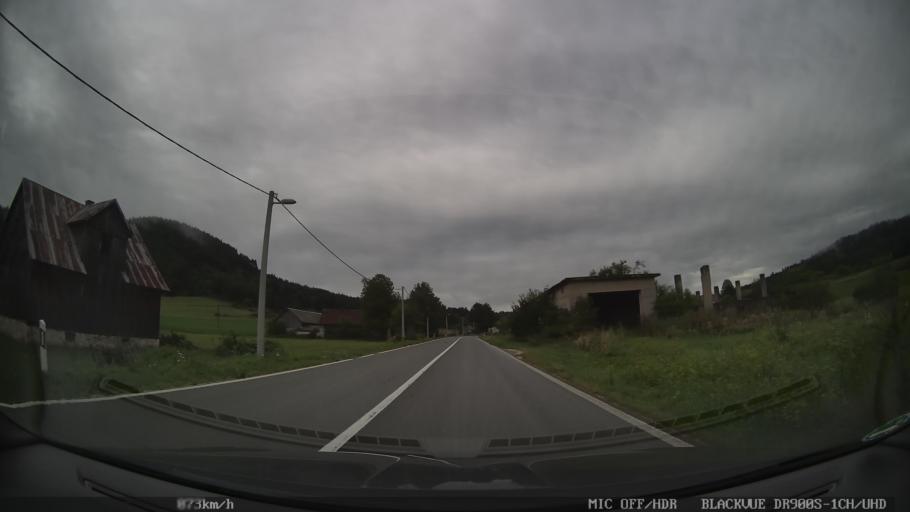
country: HR
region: Licko-Senjska
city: Jezerce
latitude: 44.8390
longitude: 15.5254
